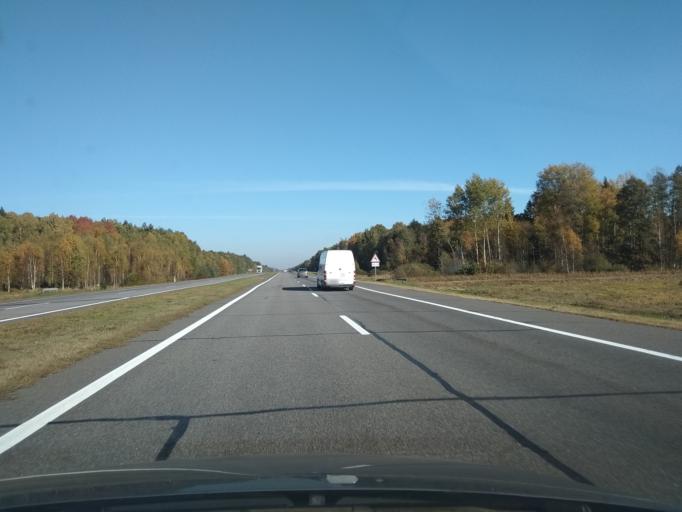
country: BY
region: Brest
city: Ivatsevichy
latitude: 52.7454
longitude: 25.4902
